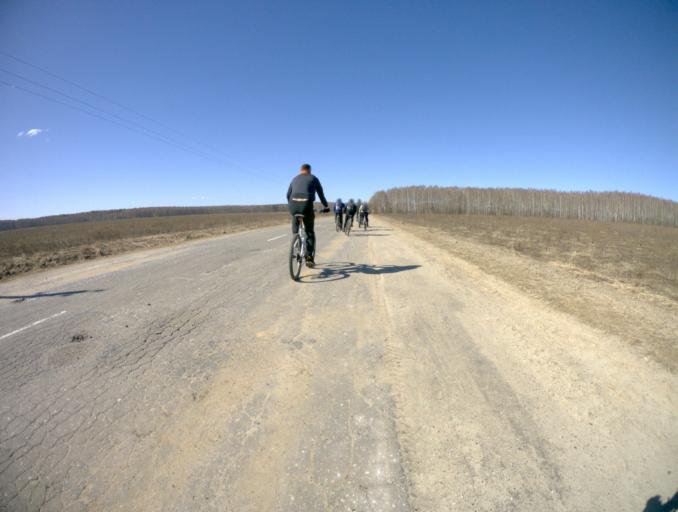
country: RU
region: Vladimir
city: Kameshkovo
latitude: 56.3465
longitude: 40.7930
